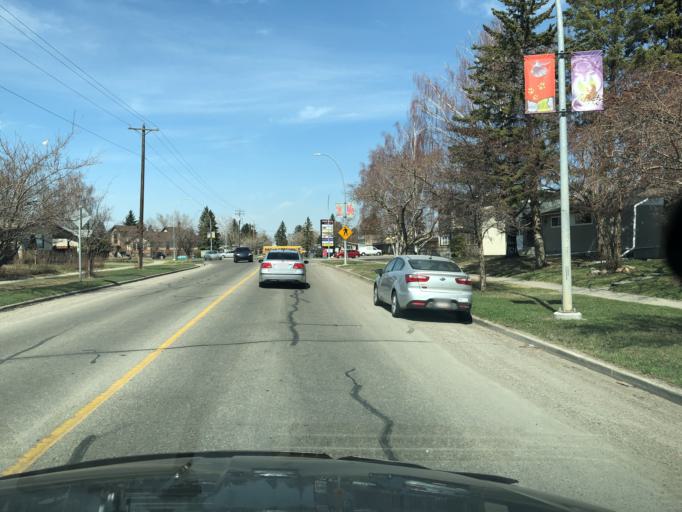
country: CA
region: Alberta
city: Calgary
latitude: 50.9687
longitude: -114.0486
